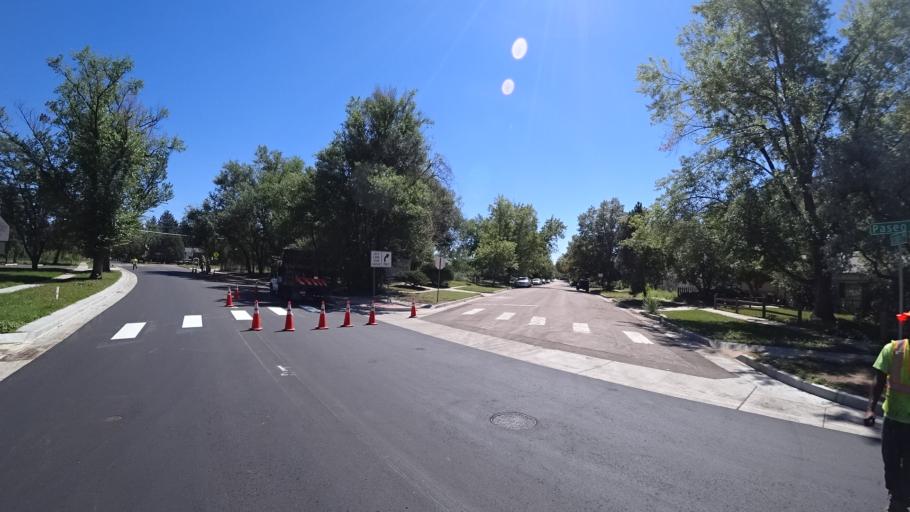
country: US
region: Colorado
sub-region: El Paso County
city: Colorado Springs
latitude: 38.8650
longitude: -104.8042
